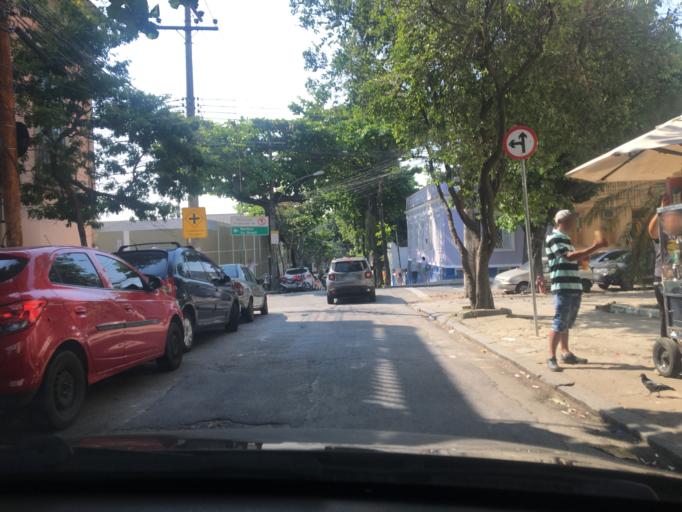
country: BR
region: Rio de Janeiro
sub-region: Rio De Janeiro
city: Rio de Janeiro
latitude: -22.8953
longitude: -43.2260
